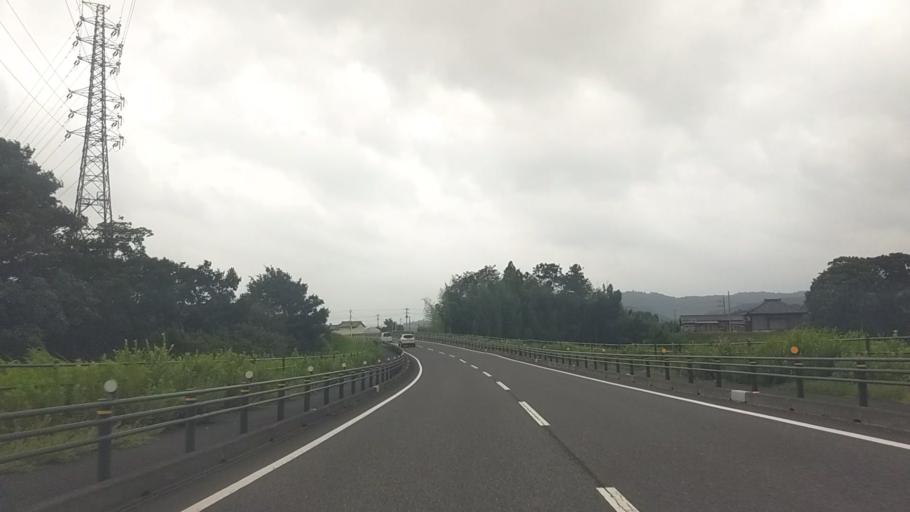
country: JP
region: Chiba
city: Kisarazu
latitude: 35.3164
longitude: 140.0546
